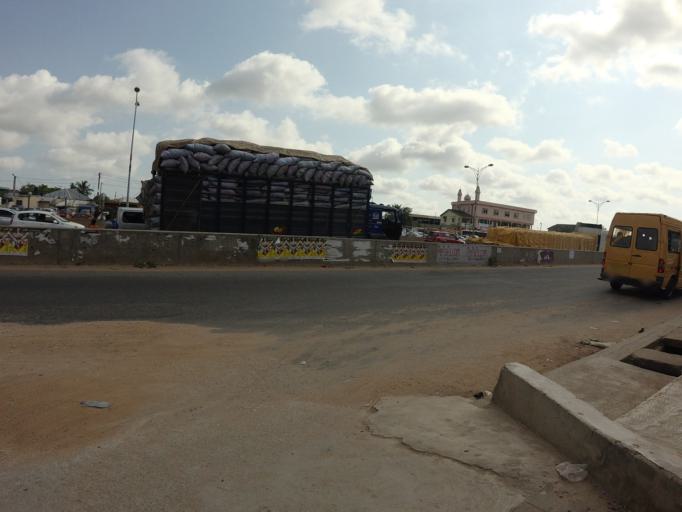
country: GH
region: Greater Accra
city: Dome
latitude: 5.6110
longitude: -0.2336
